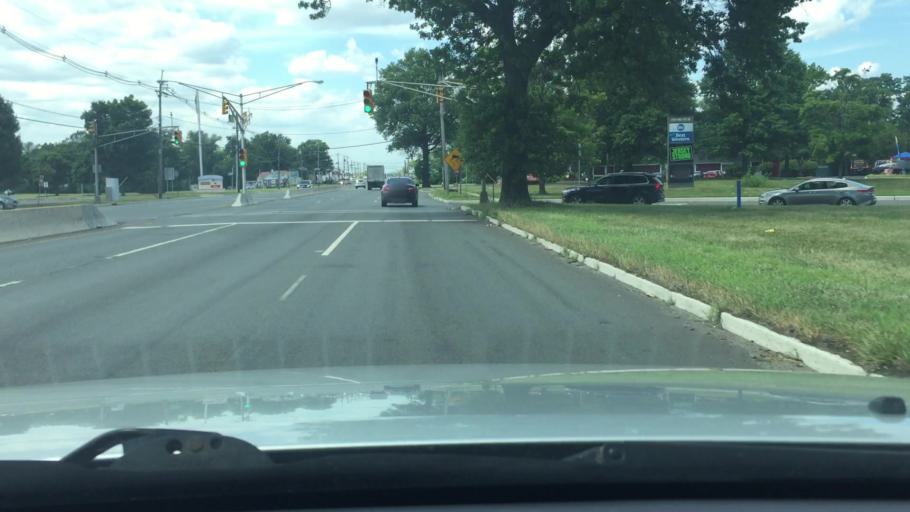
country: US
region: New Jersey
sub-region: Middlesex County
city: Old Bridge
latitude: 40.4245
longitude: -74.3795
